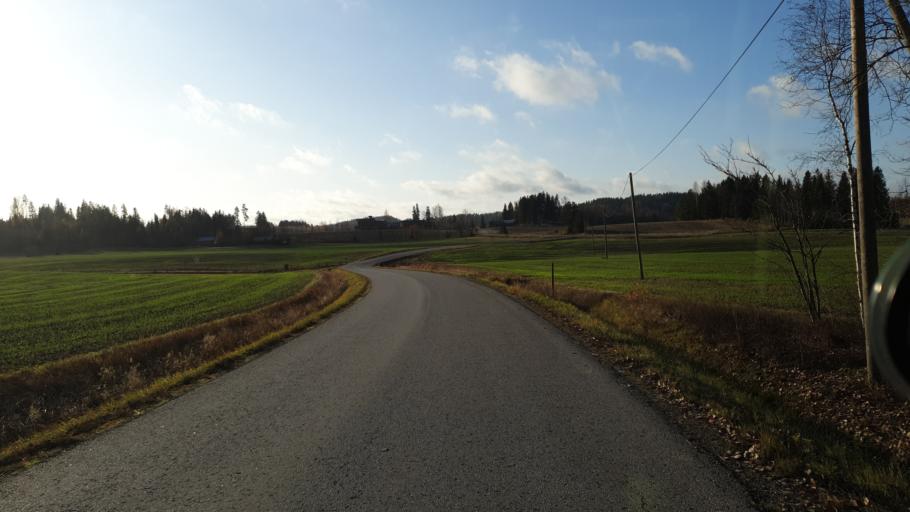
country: FI
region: Uusimaa
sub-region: Helsinki
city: Lohja
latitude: 60.2327
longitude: 24.1682
